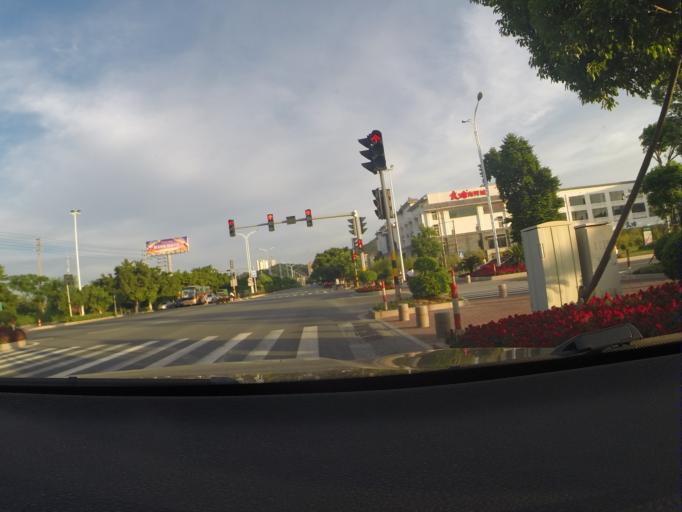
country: CN
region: Guangdong
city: Tangjiawan
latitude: 22.3436
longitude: 113.5881
